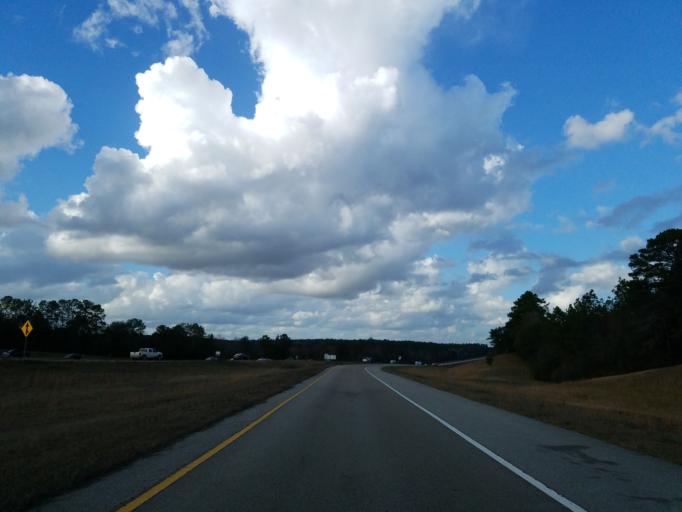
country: US
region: Mississippi
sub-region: Forrest County
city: Rawls Springs
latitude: 31.4707
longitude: -89.3222
